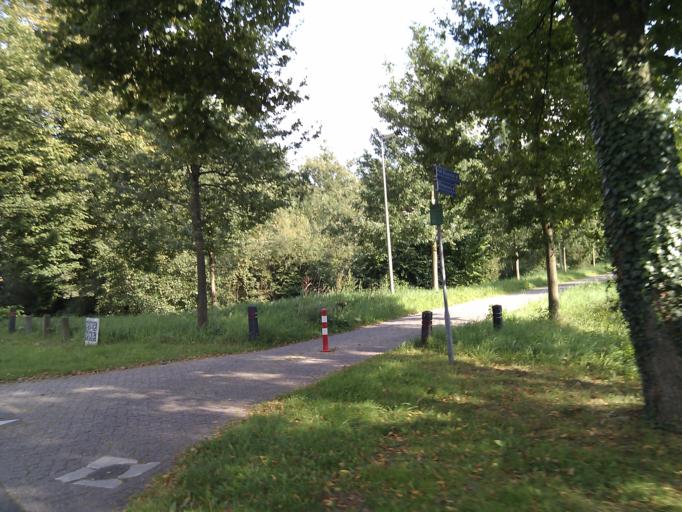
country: NL
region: Utrecht
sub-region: Gemeente Utrecht
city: Utrecht
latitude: 52.0970
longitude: 5.1494
